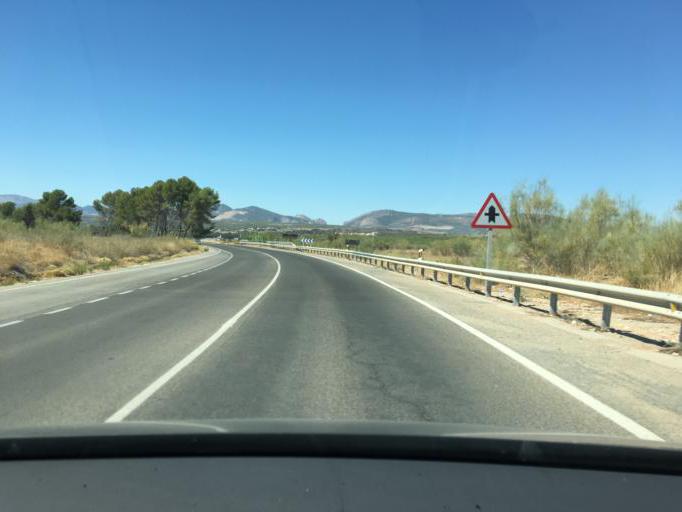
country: ES
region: Andalusia
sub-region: Provincia de Granada
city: Albolote
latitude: 37.2671
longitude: -3.6639
